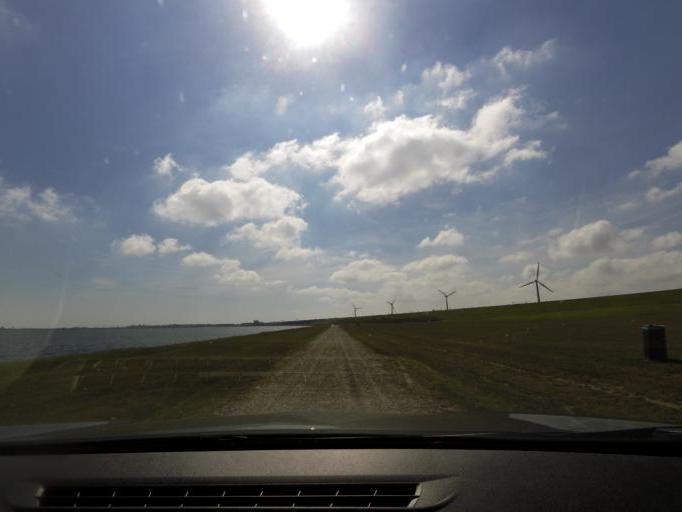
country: NL
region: South Holland
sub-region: Gemeente Hellevoetsluis
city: Nieuw-Helvoet
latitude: 51.8411
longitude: 4.0669
